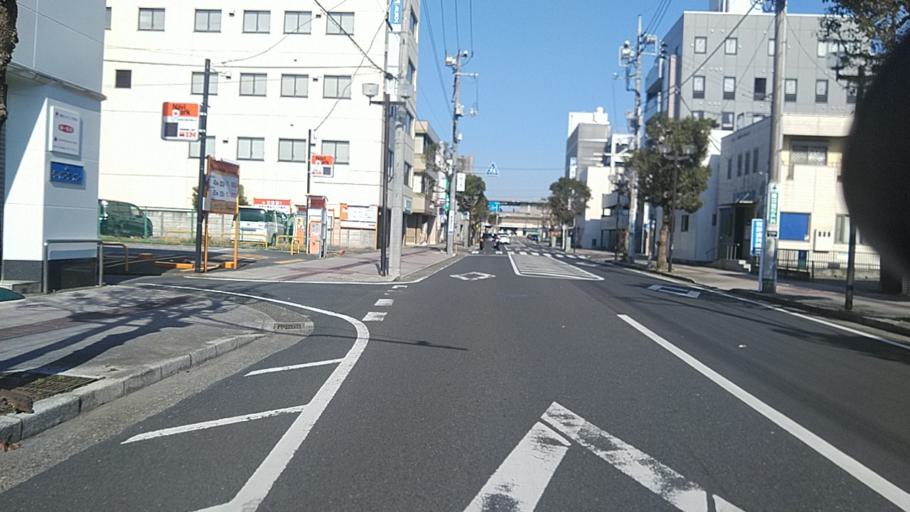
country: JP
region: Chiba
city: Mobara
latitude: 35.4250
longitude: 140.3024
